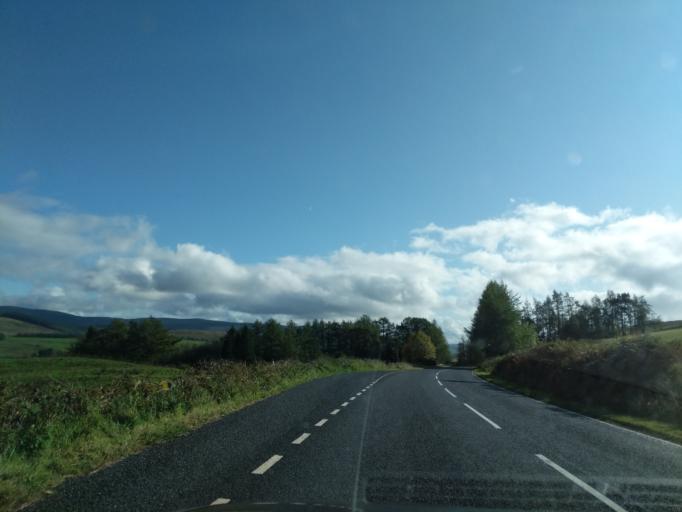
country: GB
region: Scotland
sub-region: Dumfries and Galloway
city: Moffat
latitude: 55.3576
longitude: -3.4722
